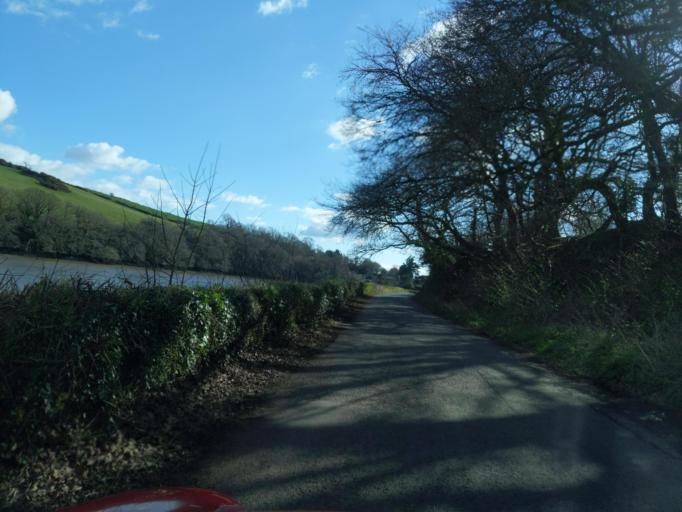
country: GB
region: England
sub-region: Devon
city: Kingsbridge
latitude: 50.2782
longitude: -3.7611
